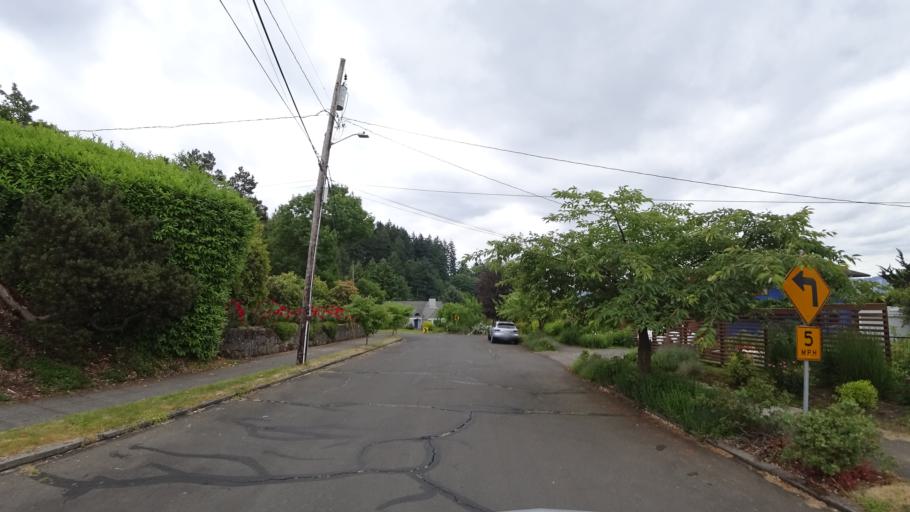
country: US
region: Oregon
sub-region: Multnomah County
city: Lents
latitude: 45.5188
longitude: -122.5968
